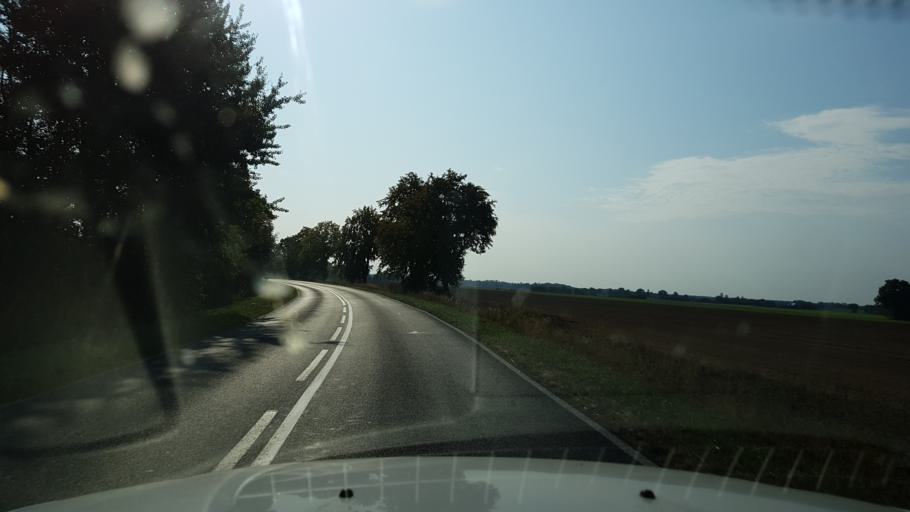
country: PL
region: West Pomeranian Voivodeship
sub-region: Powiat gryficki
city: Ploty
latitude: 53.7926
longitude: 15.2860
